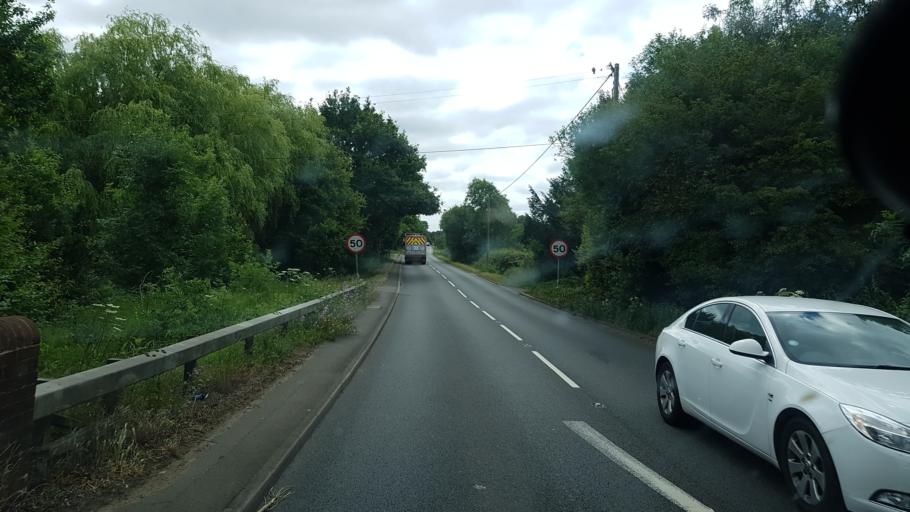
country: GB
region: England
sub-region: Surrey
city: Lingfield
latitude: 51.1891
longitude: -0.0491
